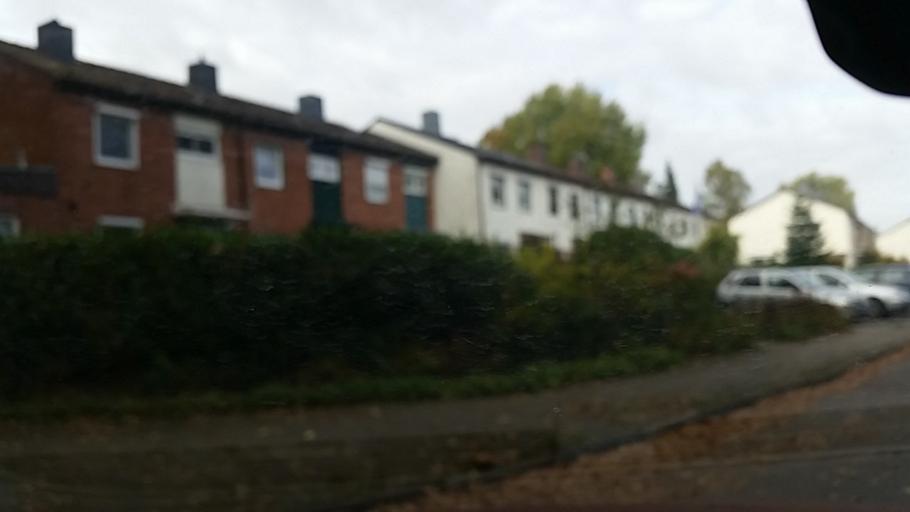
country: DE
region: Hamburg
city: Hummelsbuettel
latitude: 53.6556
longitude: 10.0283
